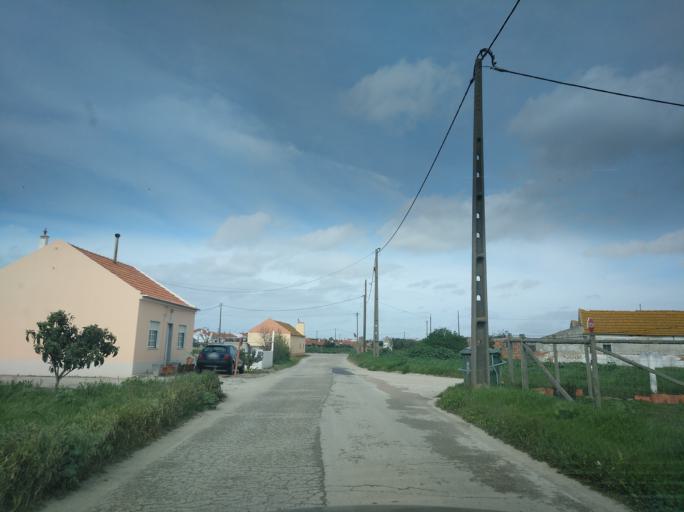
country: PT
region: Setubal
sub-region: Palmela
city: Pinhal Novo
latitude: 38.6706
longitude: -8.9220
